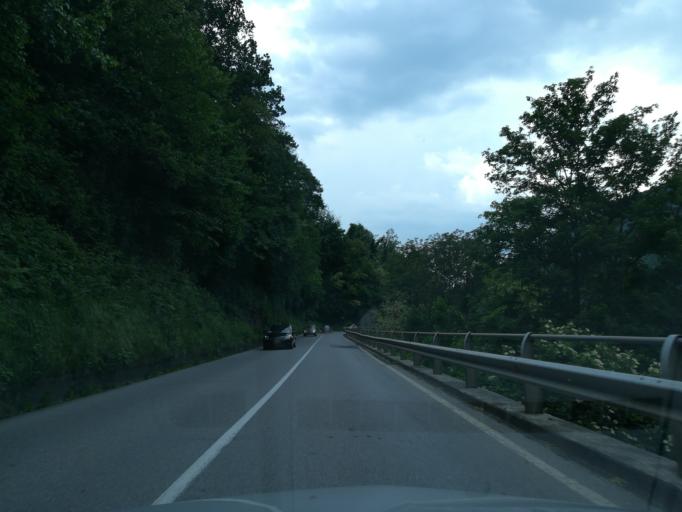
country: IT
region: Lombardy
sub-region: Provincia di Bergamo
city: Almenno San Salvatore
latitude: 45.7591
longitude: 9.5958
